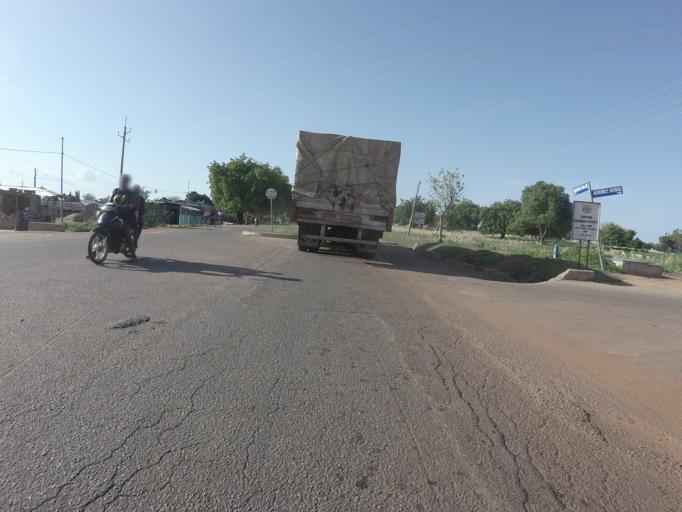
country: GH
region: Upper East
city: Navrongo
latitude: 10.9010
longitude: -1.0922
